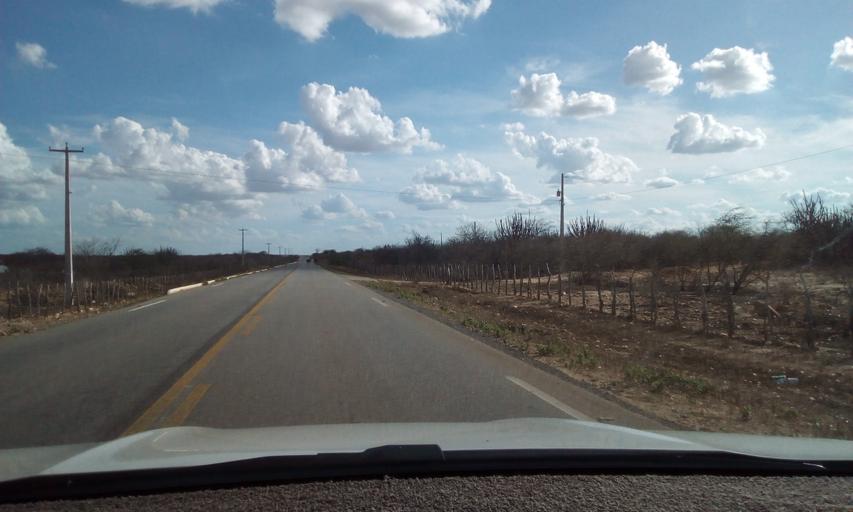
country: BR
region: Paraiba
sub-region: Soledade
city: Soledade
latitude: -6.8048
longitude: -36.4031
